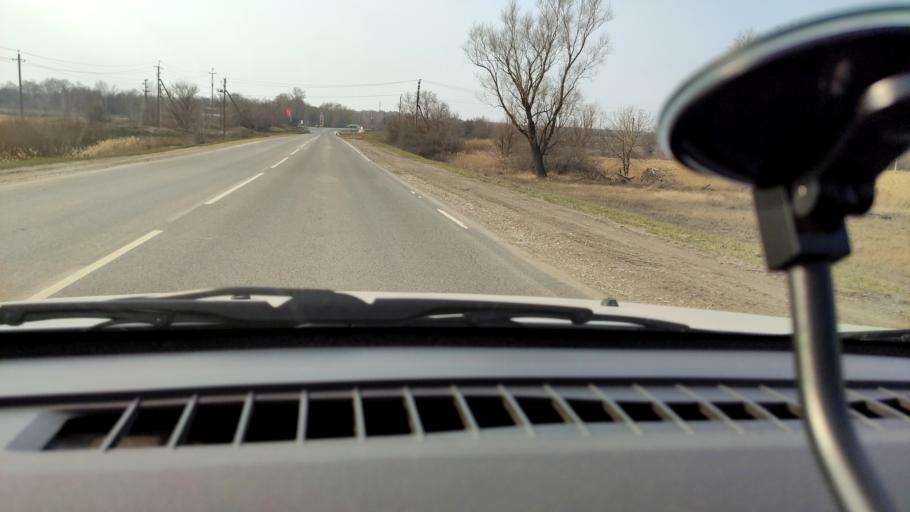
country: RU
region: Samara
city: Dubovyy Umet
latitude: 53.0642
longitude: 50.3730
